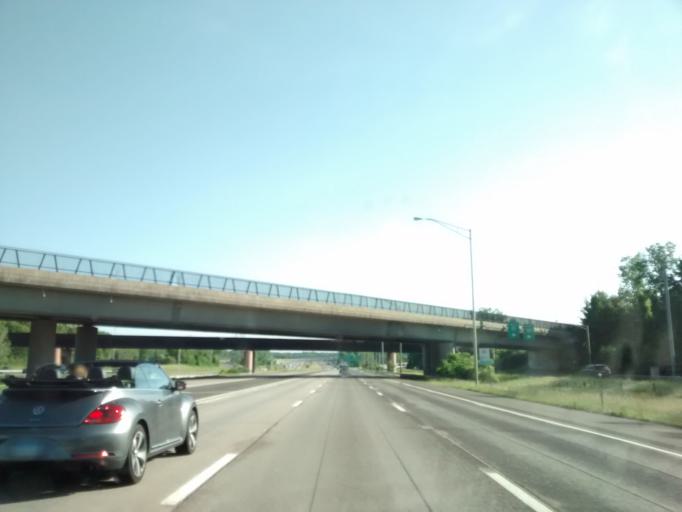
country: US
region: Connecticut
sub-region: Hartford County
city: Manchester
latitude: 41.7966
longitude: -72.5589
